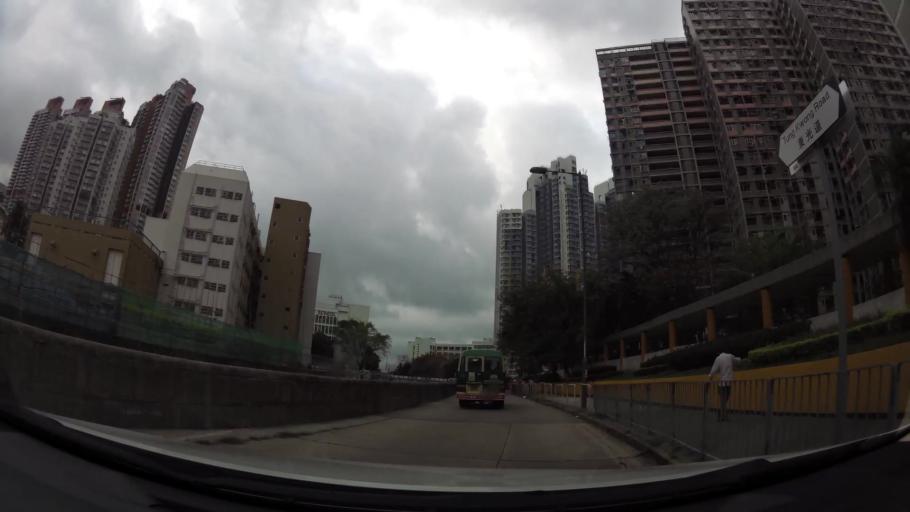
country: HK
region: Wong Tai Sin
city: Wong Tai Sin
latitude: 22.3343
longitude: 114.1939
